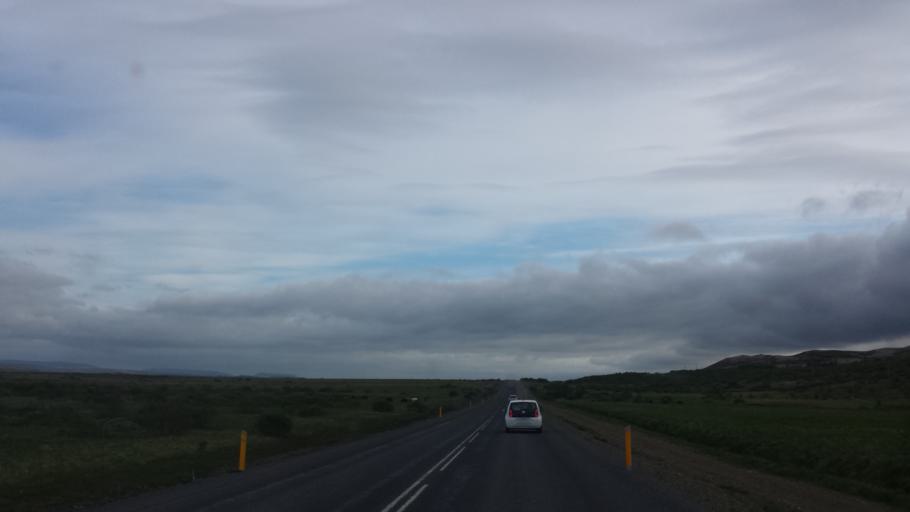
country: IS
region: South
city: Selfoss
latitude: 64.2949
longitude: -20.3348
